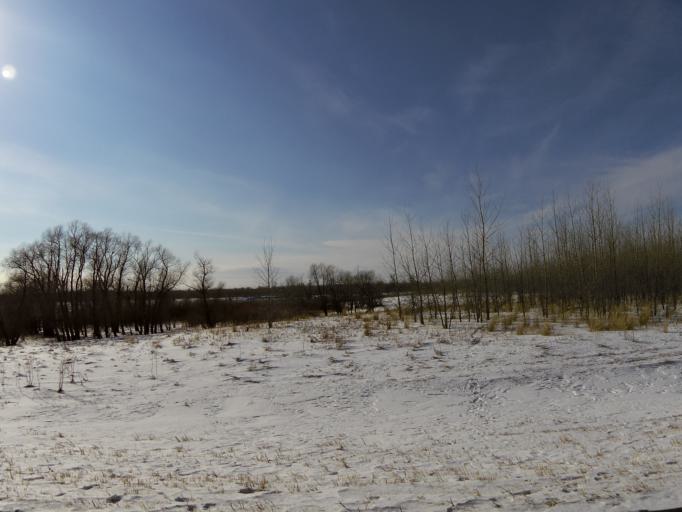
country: US
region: North Dakota
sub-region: Walsh County
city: Grafton
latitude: 48.4220
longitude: -97.1073
